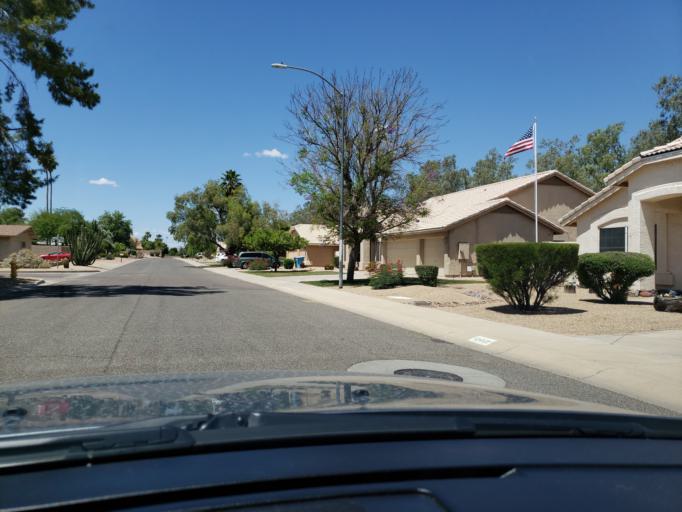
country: US
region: Arizona
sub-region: Maricopa County
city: Paradise Valley
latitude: 33.6094
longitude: -112.0176
